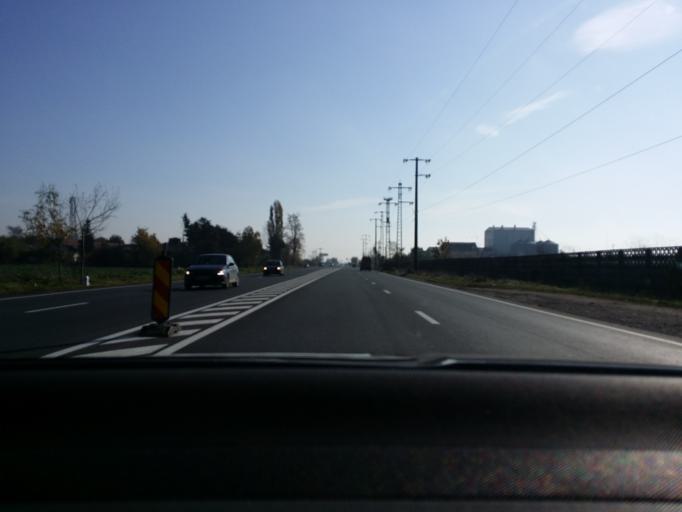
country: RO
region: Prahova
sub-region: Comuna Paulesti
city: Gageni
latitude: 44.9891
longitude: 25.9149
